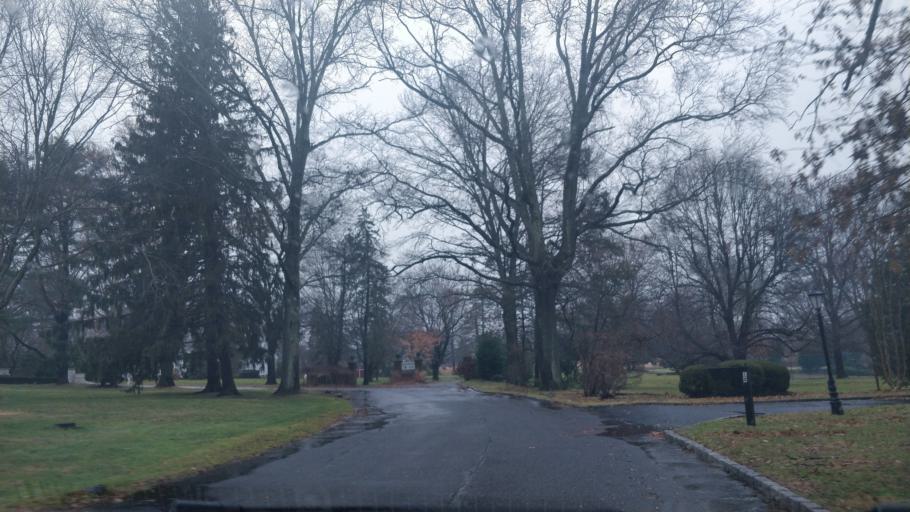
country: US
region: New York
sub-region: Nassau County
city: Old Brookville
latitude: 40.8376
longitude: -73.6000
